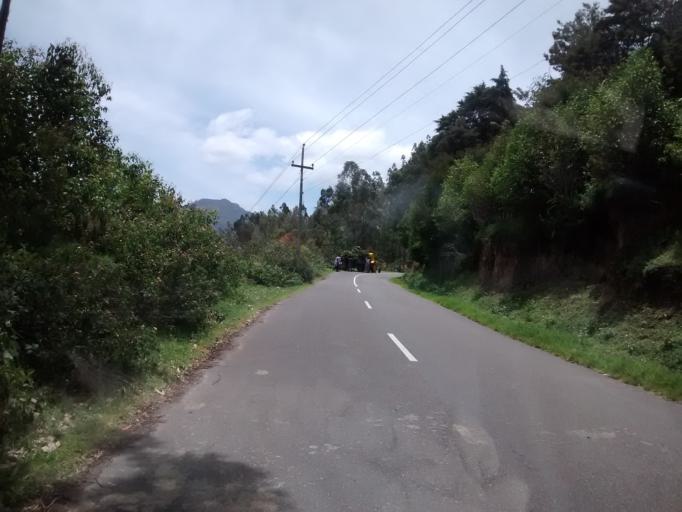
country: IN
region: Kerala
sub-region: Idukki
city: Munnar
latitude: 10.1355
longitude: 77.1783
